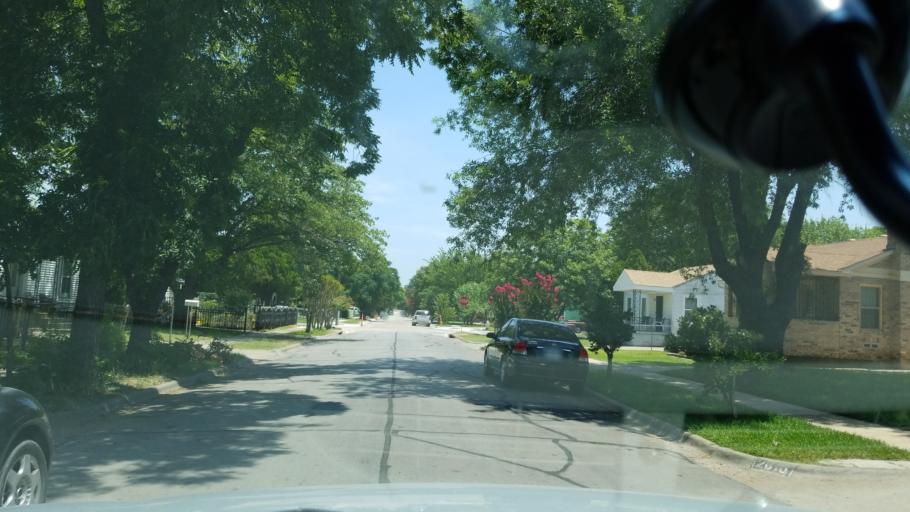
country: US
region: Texas
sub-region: Dallas County
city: Cockrell Hill
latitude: 32.7283
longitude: -96.8622
